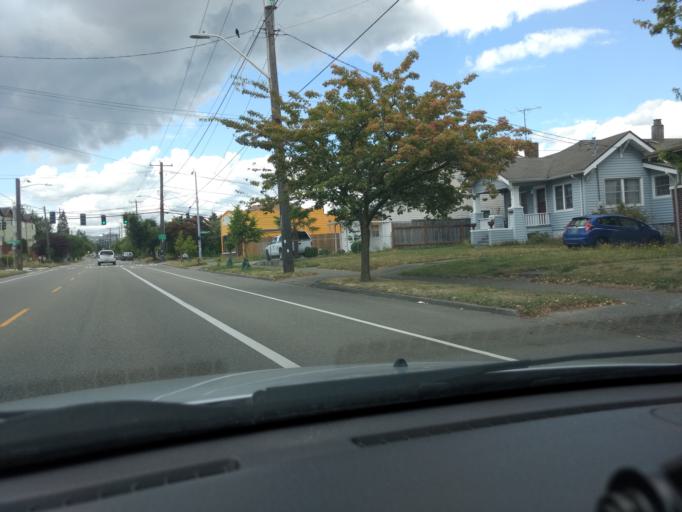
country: US
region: Washington
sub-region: King County
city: Riverton
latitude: 47.5306
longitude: -122.2785
